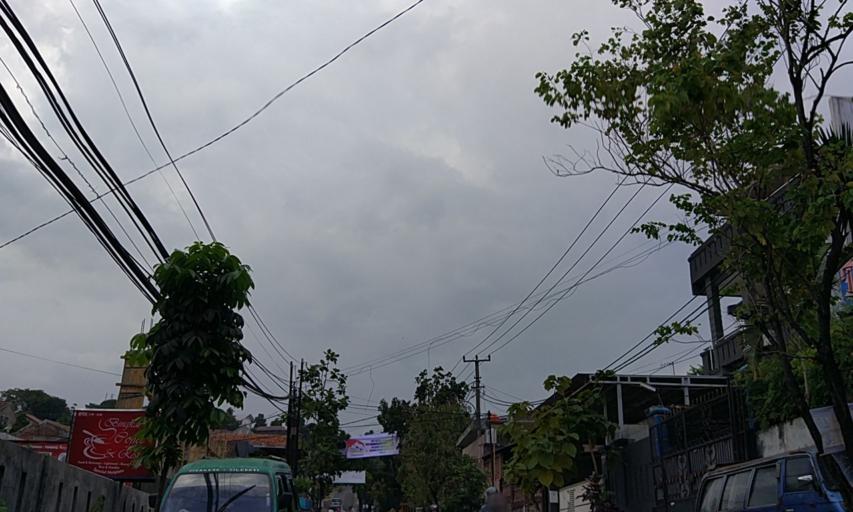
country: ID
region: West Java
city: Bandung
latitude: -6.9026
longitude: 107.6802
